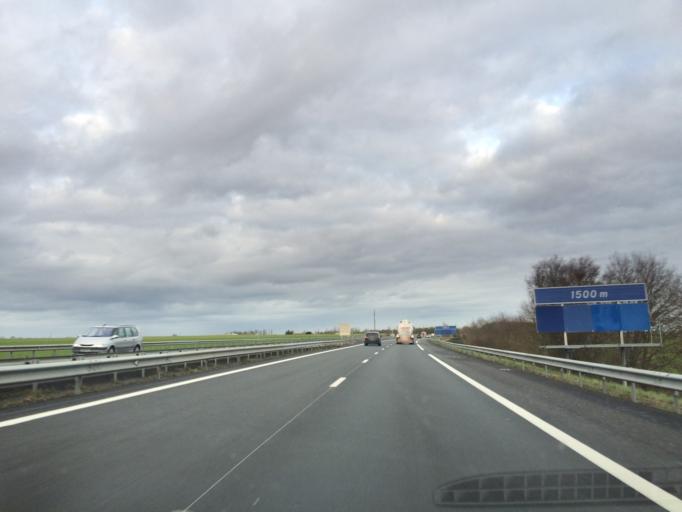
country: FR
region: Poitou-Charentes
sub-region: Departement des Deux-Sevres
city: Aiffres
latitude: 46.2890
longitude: -0.3908
